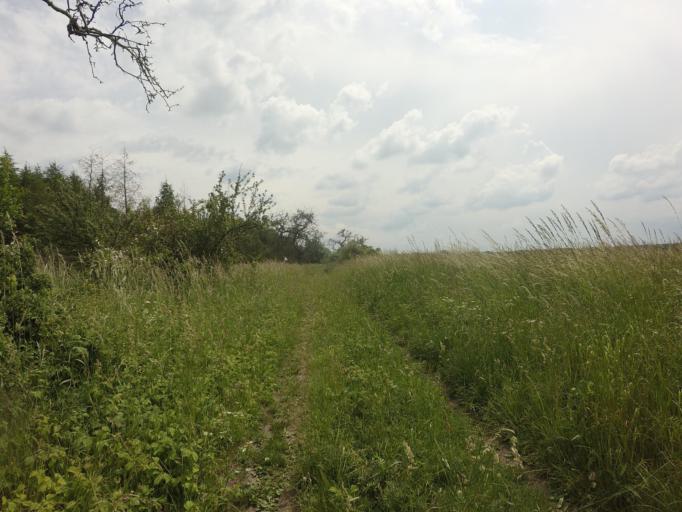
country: PL
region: West Pomeranian Voivodeship
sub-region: Powiat stargardzki
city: Dobrzany
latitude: 53.3400
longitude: 15.4424
